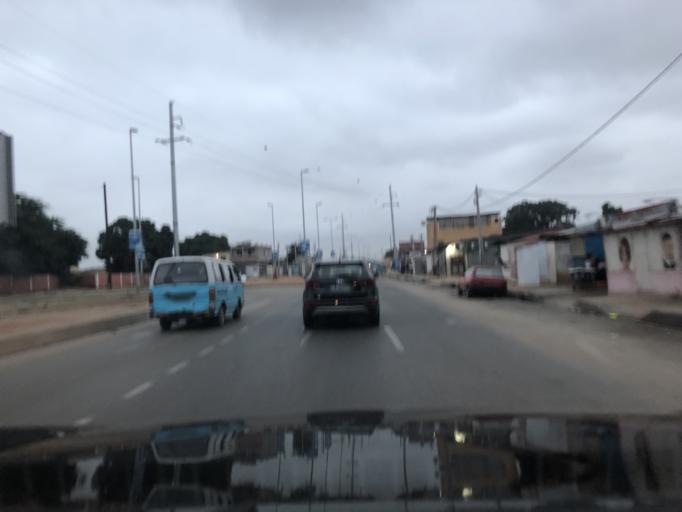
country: AO
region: Luanda
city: Luanda
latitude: -8.8418
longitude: 13.2440
